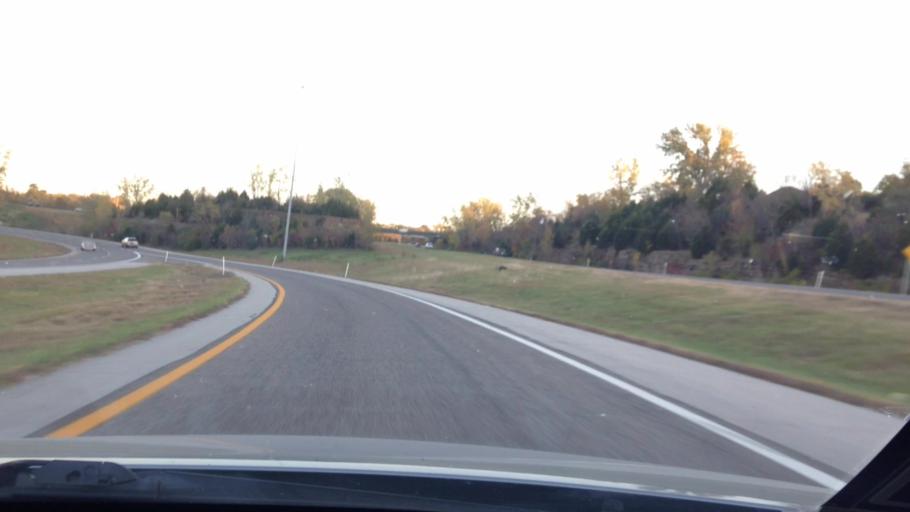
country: US
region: Kansas
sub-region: Wyandotte County
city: Edwardsville
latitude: 39.1054
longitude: -94.8148
